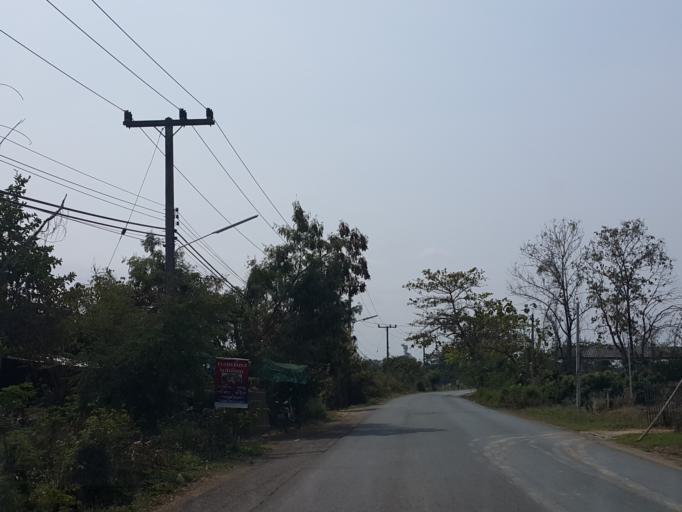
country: TH
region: Lamphun
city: Ban Thi
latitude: 18.6721
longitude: 99.0990
